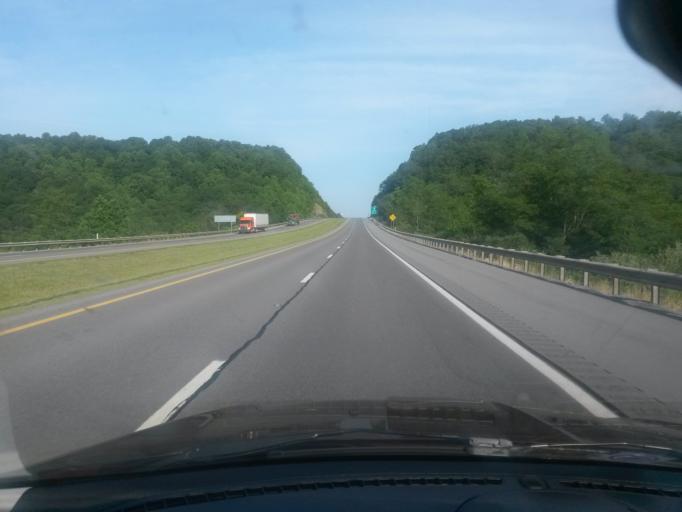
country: US
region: West Virginia
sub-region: Greenbrier County
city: Lewisburg
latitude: 37.8630
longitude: -80.5375
